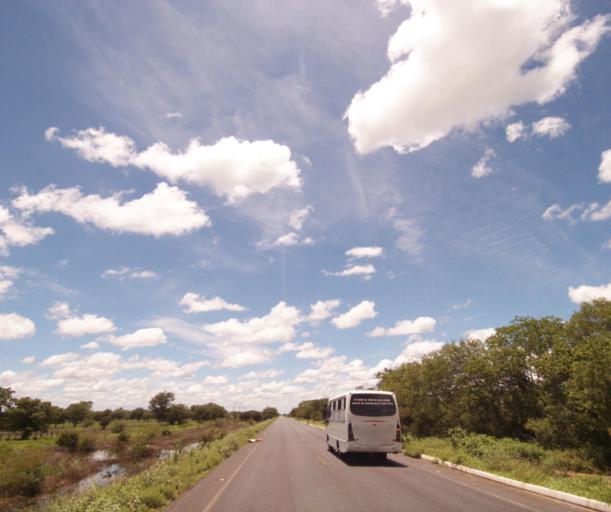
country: BR
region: Bahia
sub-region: Bom Jesus Da Lapa
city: Bom Jesus da Lapa
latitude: -13.2598
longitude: -43.4969
